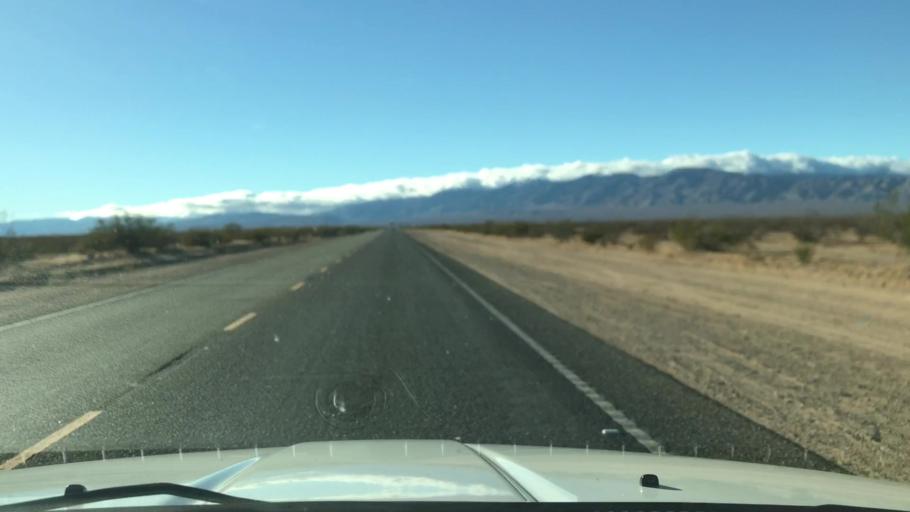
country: US
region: California
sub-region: Kern County
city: California City
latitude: 35.1256
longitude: -118.0322
